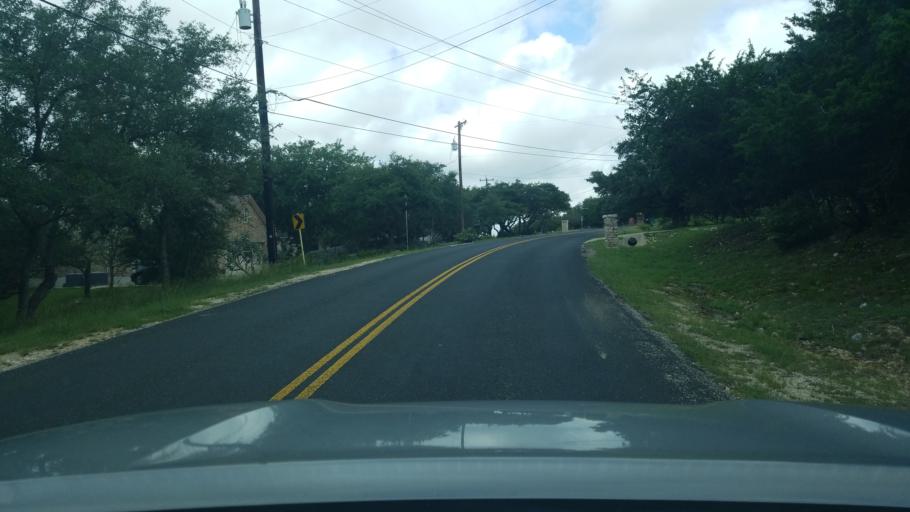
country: US
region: Texas
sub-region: Bexar County
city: Timberwood Park
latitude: 29.6846
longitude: -98.4900
